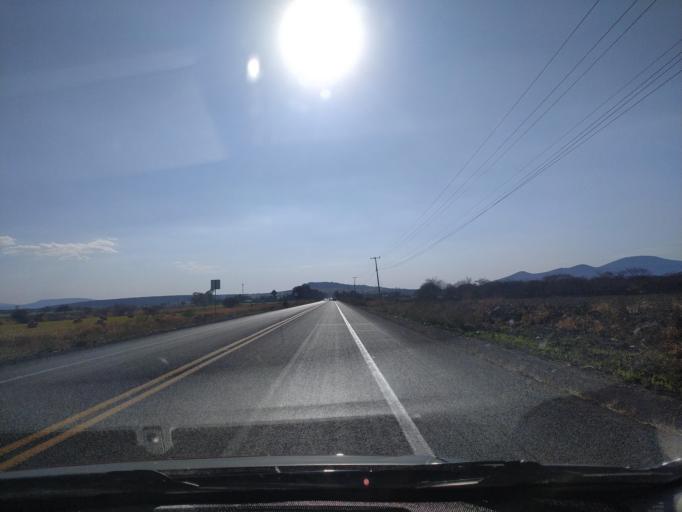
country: MX
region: Michoacan
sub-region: Yurecuaro
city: Yurecuaro
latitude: 20.3432
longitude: -102.1634
